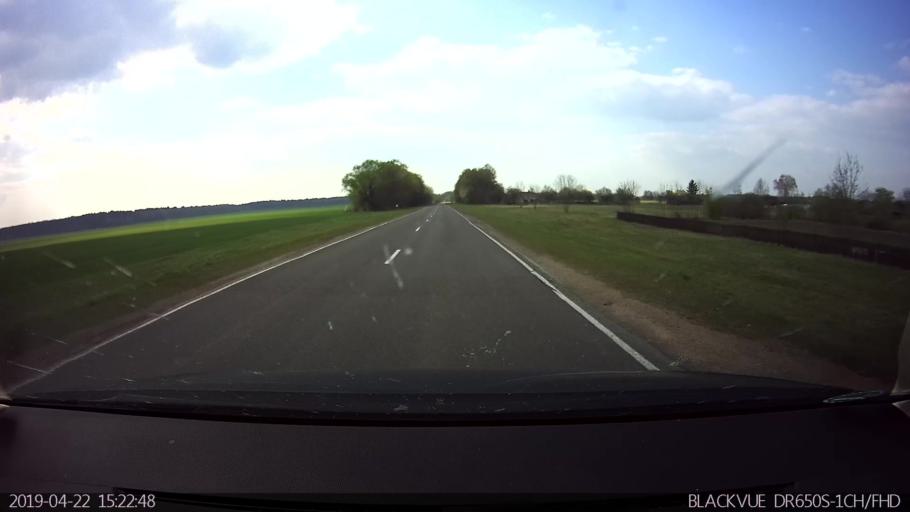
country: BY
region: Brest
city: Vysokaye
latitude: 52.3518
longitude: 23.4386
